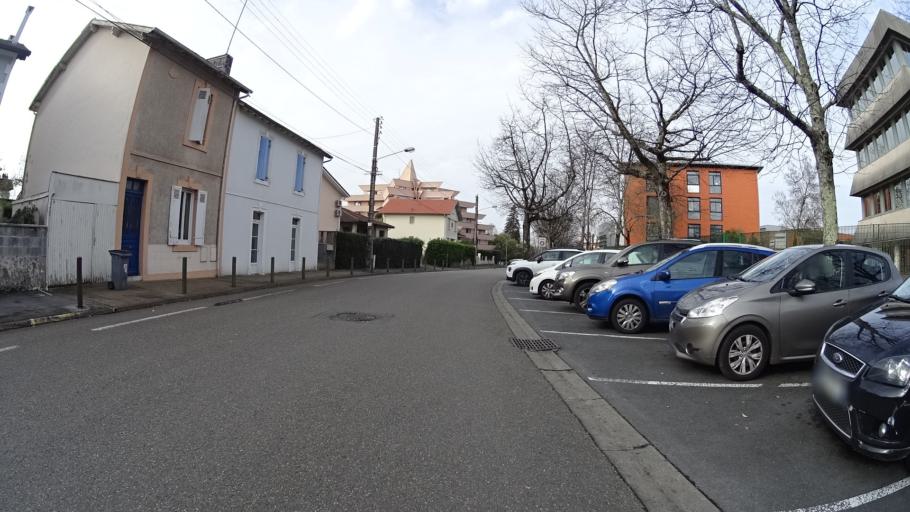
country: FR
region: Aquitaine
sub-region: Departement des Landes
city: Dax
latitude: 43.7012
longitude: -1.0562
